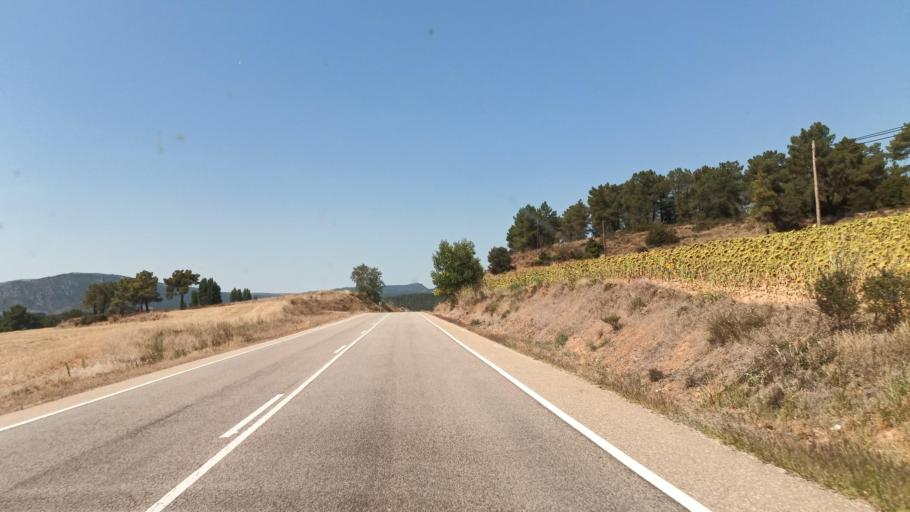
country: ES
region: Castille and Leon
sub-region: Provincia de Burgos
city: Salas de Bureba
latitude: 42.6729
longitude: -3.4178
